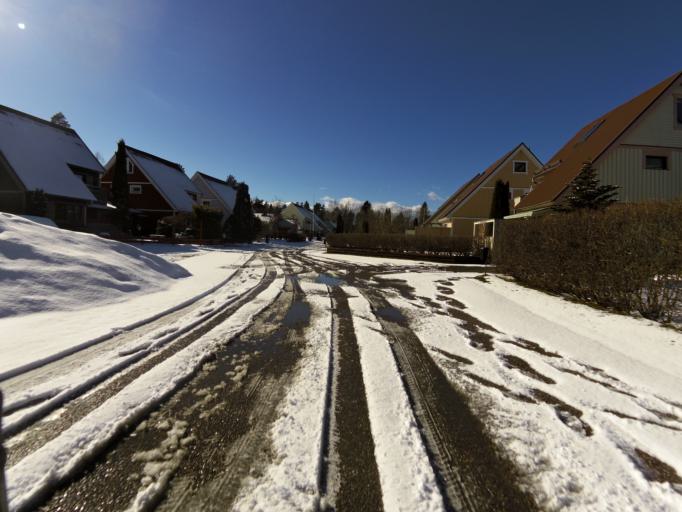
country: SE
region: Gaevleborg
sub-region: Gavle Kommun
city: Gavle
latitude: 60.6610
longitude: 17.2187
